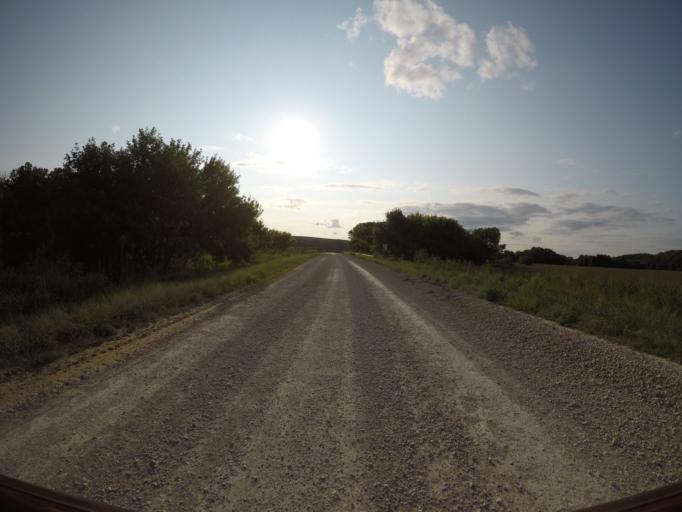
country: US
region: Kansas
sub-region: Wabaunsee County
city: Alma
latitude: 38.9515
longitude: -96.2442
